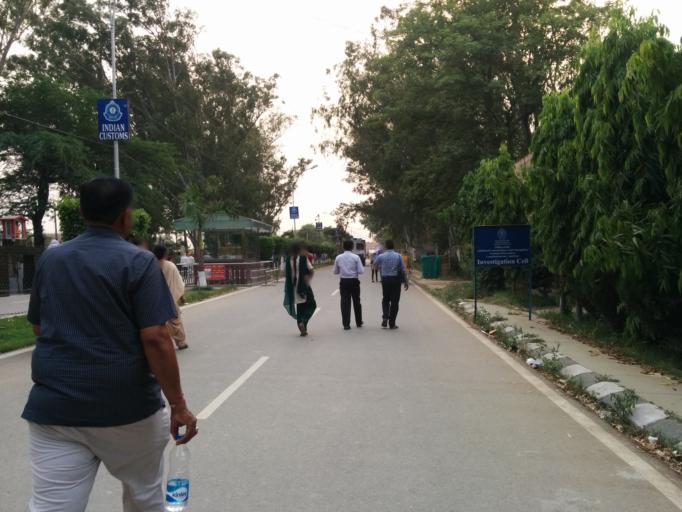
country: PK
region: Punjab
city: Lahore
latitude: 31.6052
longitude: 74.5779
